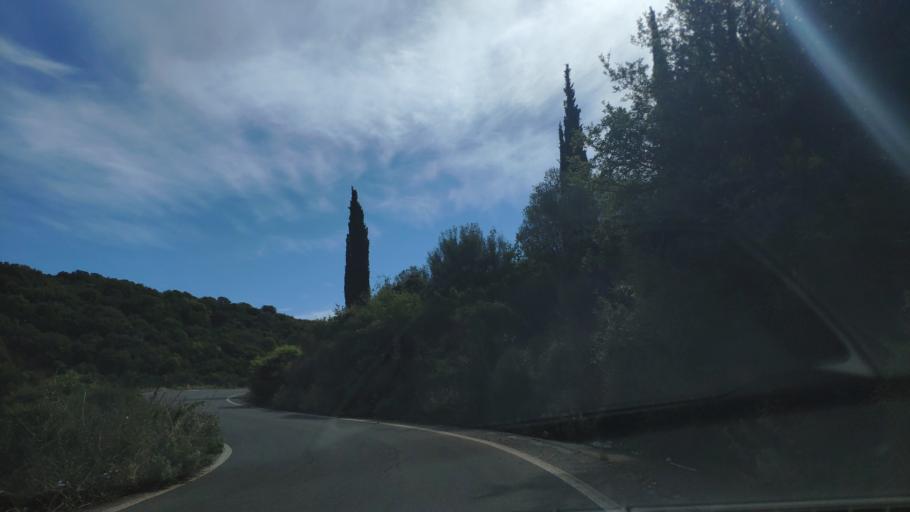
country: GR
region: Peloponnese
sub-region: Nomos Arkadias
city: Dimitsana
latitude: 37.5266
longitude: 22.0702
